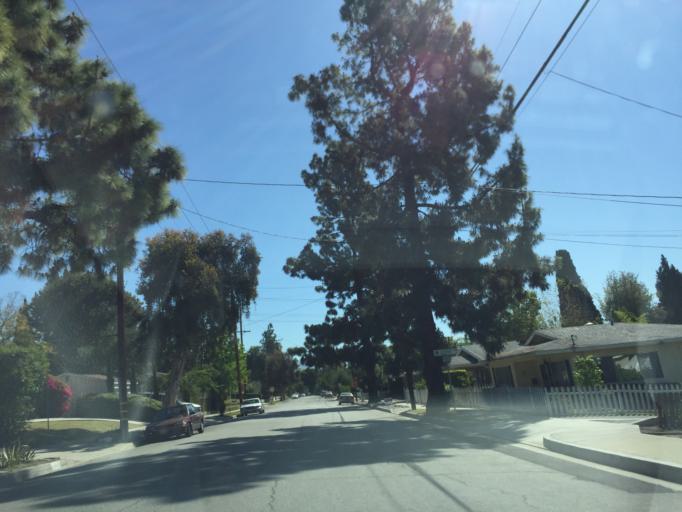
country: US
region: California
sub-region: Los Angeles County
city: Sierra Madre
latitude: 34.1642
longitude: -118.0610
